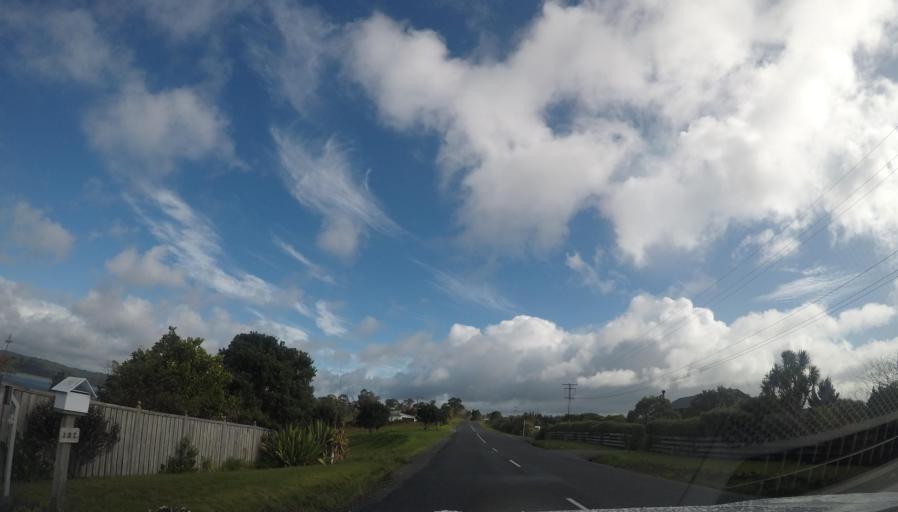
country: NZ
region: Auckland
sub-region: Auckland
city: Warkworth
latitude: -36.4649
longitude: 174.7353
